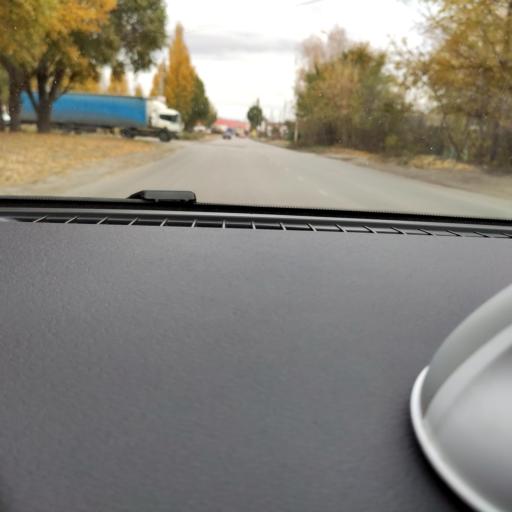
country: RU
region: Samara
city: Petra-Dubrava
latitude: 53.2503
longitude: 50.3101
